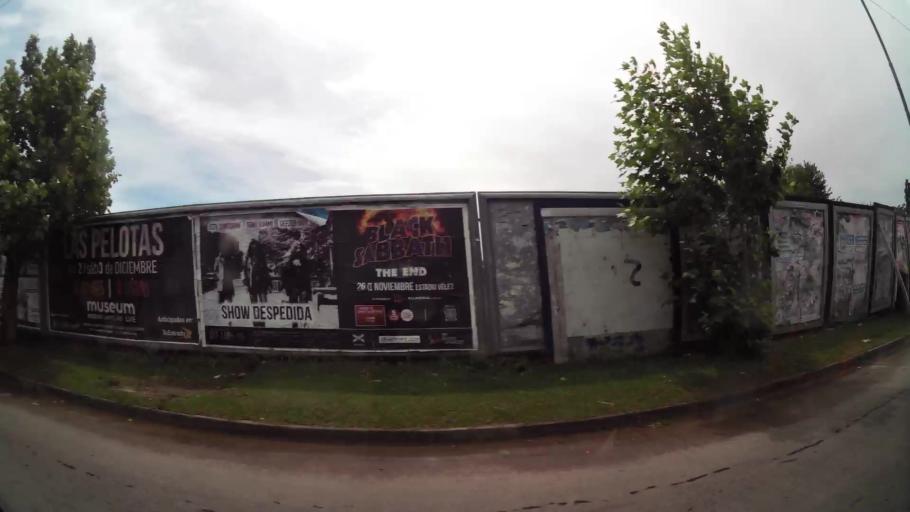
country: AR
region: Buenos Aires F.D.
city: Villa Lugano
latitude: -34.6769
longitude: -58.4636
